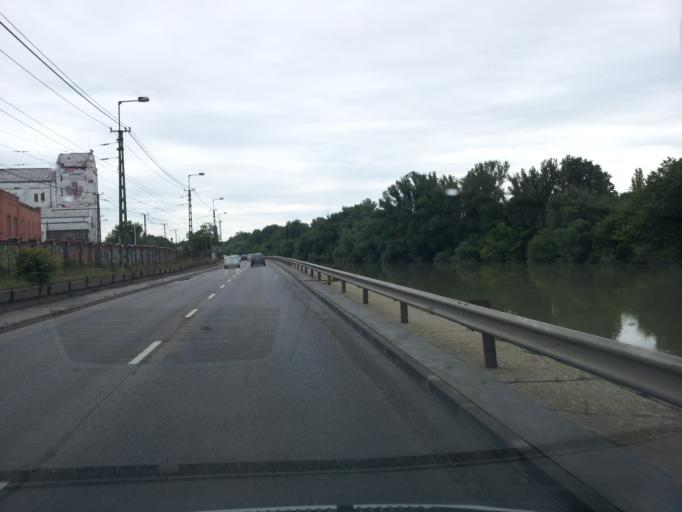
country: HU
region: Budapest
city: Budapest III. keruelet
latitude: 47.5464
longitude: 19.0474
